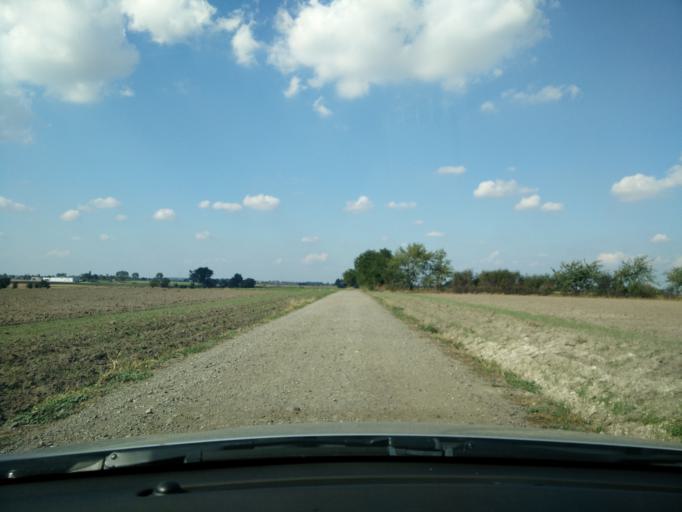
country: PL
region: Greater Poland Voivodeship
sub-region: Powiat poznanski
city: Kleszczewo
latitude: 52.2605
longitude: 17.1871
